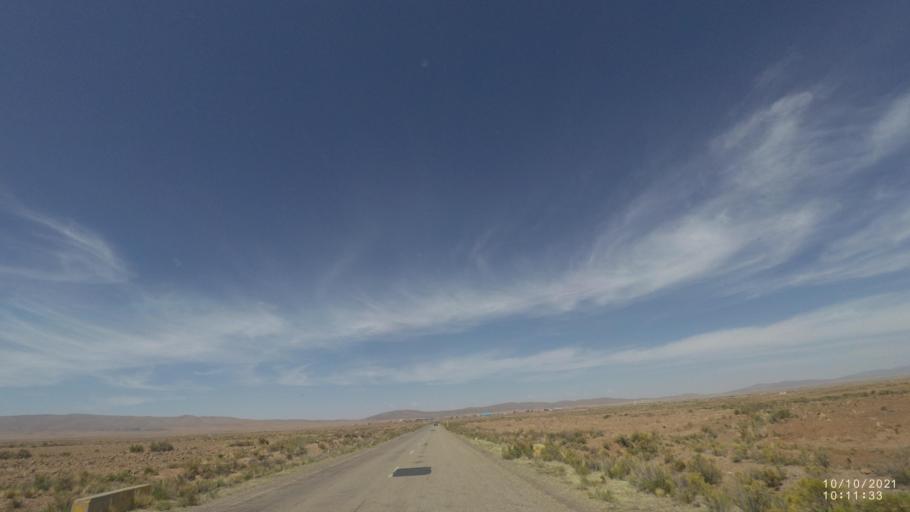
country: BO
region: La Paz
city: Eucaliptus
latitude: -17.4243
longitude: -67.5050
